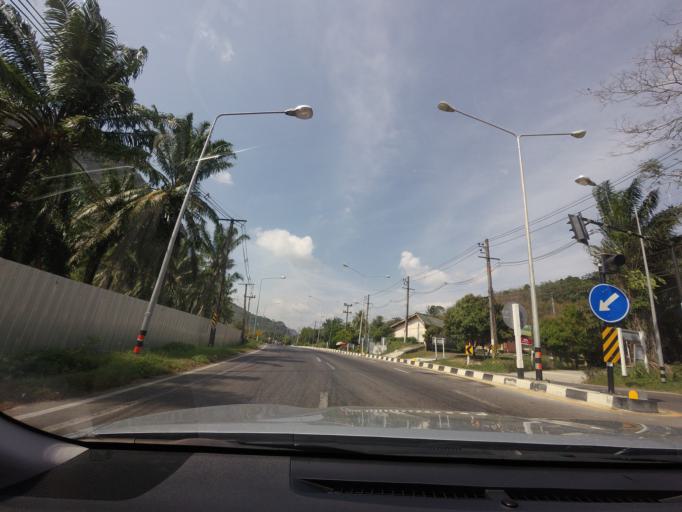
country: TH
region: Phangnga
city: Ban Ao Nang
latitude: 8.0796
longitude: 98.8045
